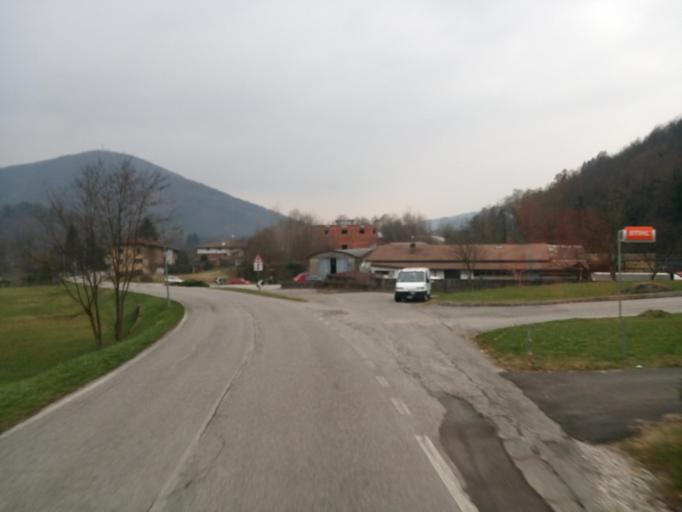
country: IT
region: Friuli Venezia Giulia
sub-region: Provincia di Udine
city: Merso di Sopra
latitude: 46.1169
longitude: 13.5082
